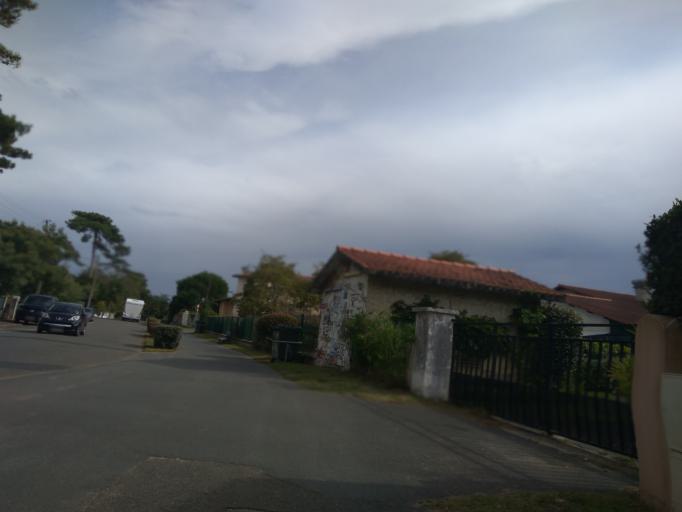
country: FR
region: Aquitaine
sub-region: Departement des Landes
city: Capbreton
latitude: 43.6399
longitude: -1.4399
